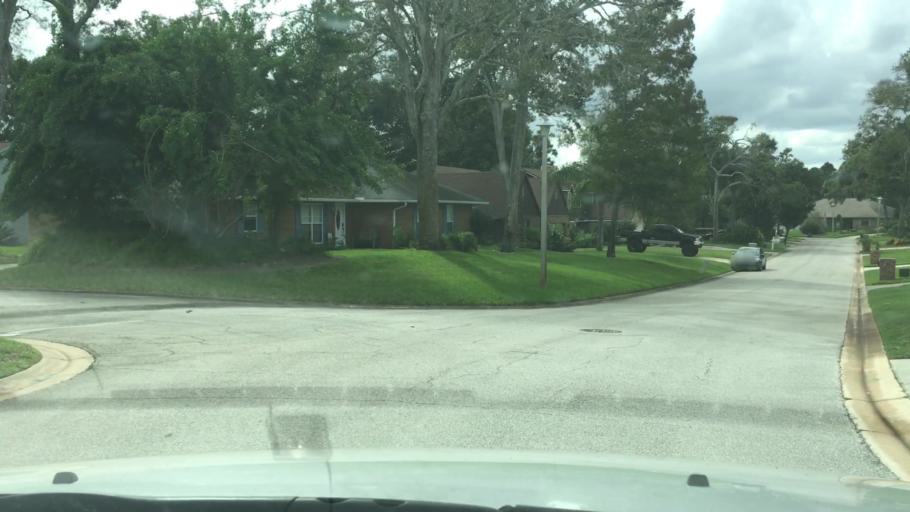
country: US
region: Florida
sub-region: Volusia County
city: Ormond-by-the-Sea
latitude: 29.3200
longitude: -81.0752
